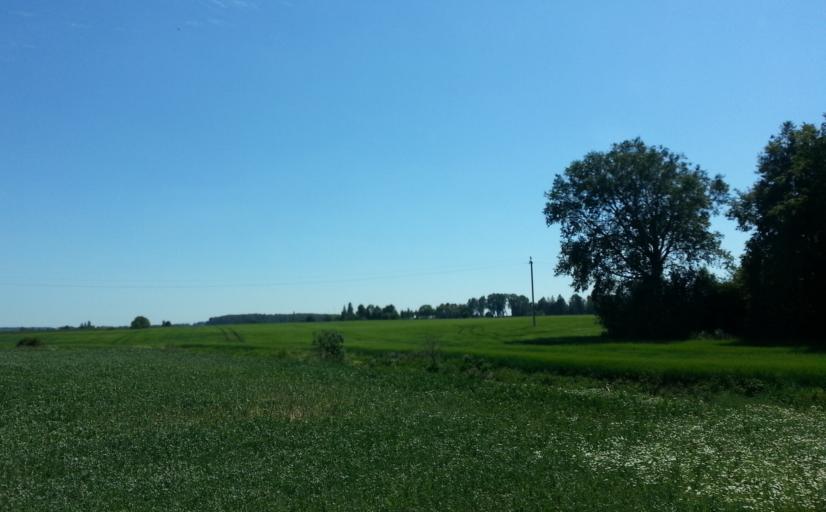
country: LT
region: Panevezys
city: Pasvalys
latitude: 56.2274
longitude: 24.4380
